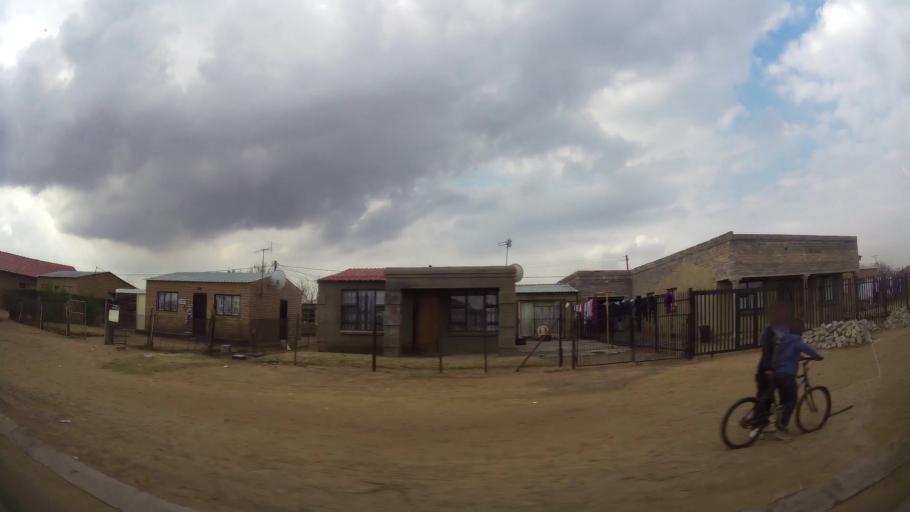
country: ZA
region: Orange Free State
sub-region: Fezile Dabi District Municipality
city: Sasolburg
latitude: -26.8562
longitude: 27.8562
